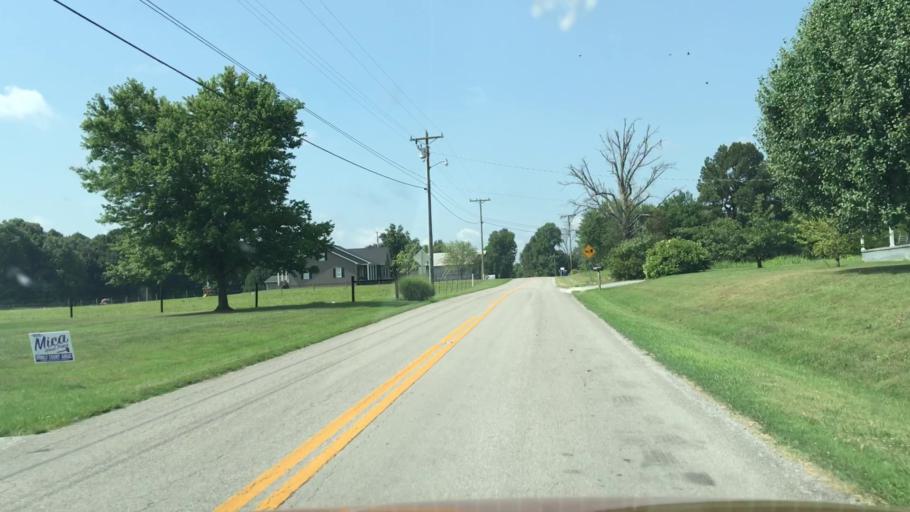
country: US
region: Kentucky
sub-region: Barren County
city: Glasgow
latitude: 36.8831
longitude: -85.8460
